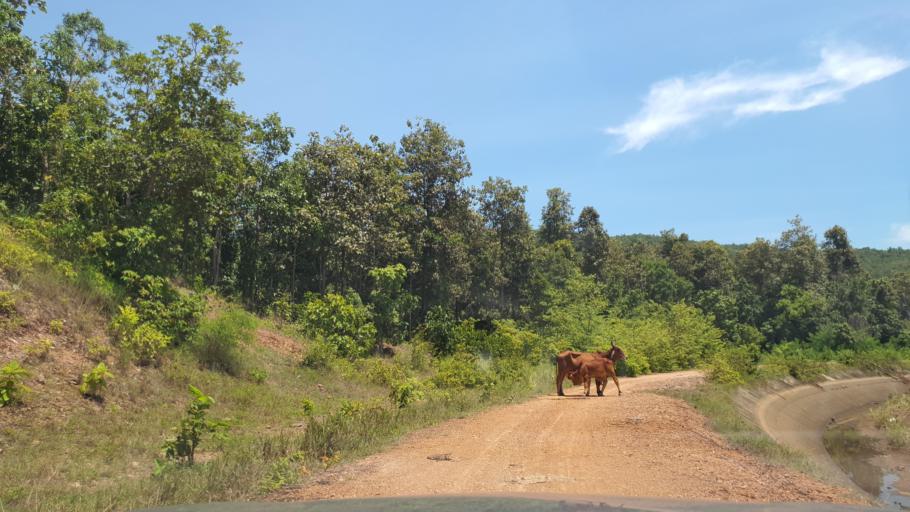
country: TH
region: Chiang Mai
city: Mae On
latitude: 18.7767
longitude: 99.1899
